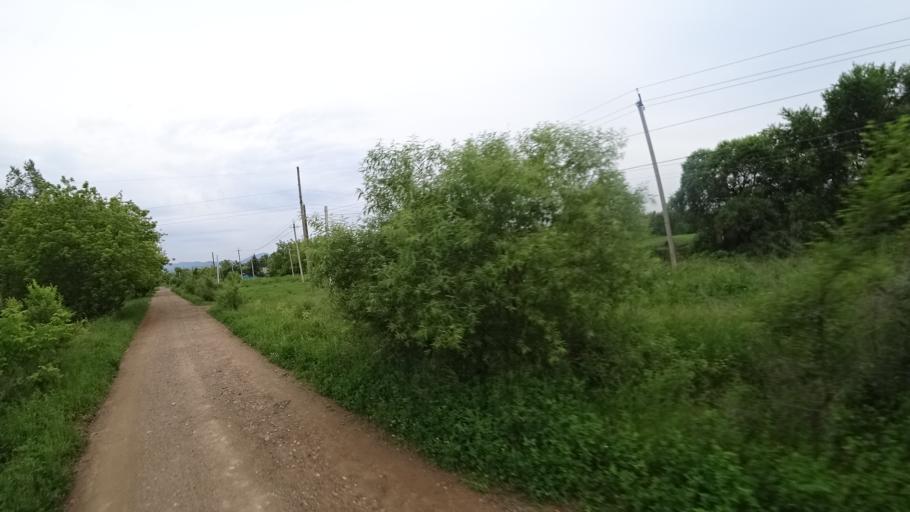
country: RU
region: Primorskiy
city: Novosysoyevka
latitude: 44.2327
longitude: 133.3654
